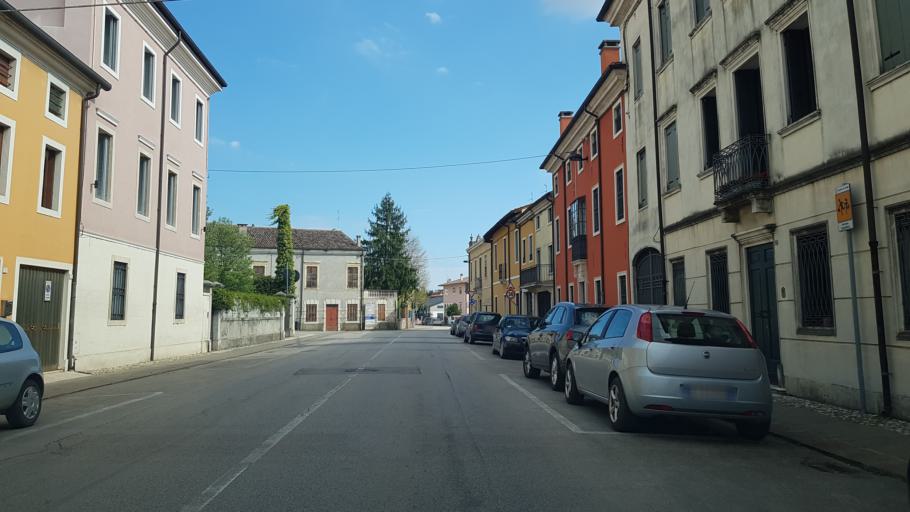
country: IT
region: Veneto
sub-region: Provincia di Vicenza
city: Lonigo
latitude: 45.3887
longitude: 11.3923
